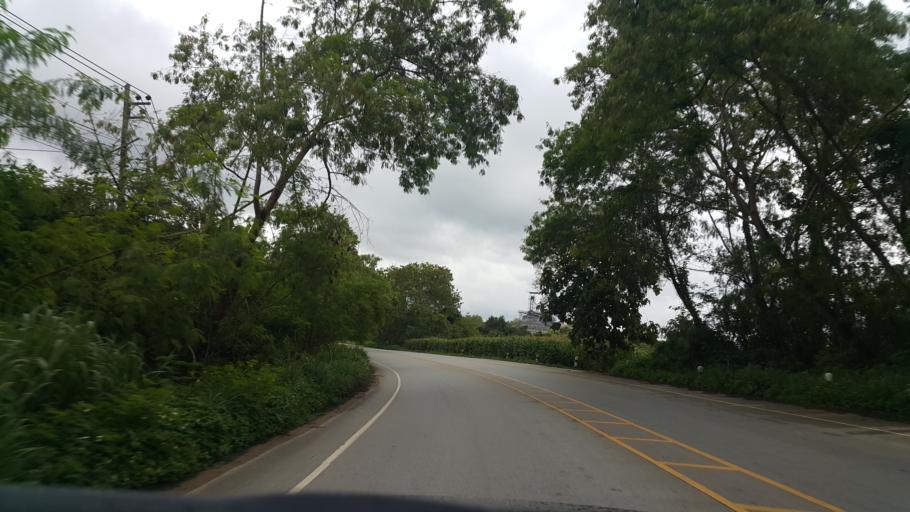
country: TH
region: Lampang
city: Wang Nuea
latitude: 19.1925
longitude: 99.5334
